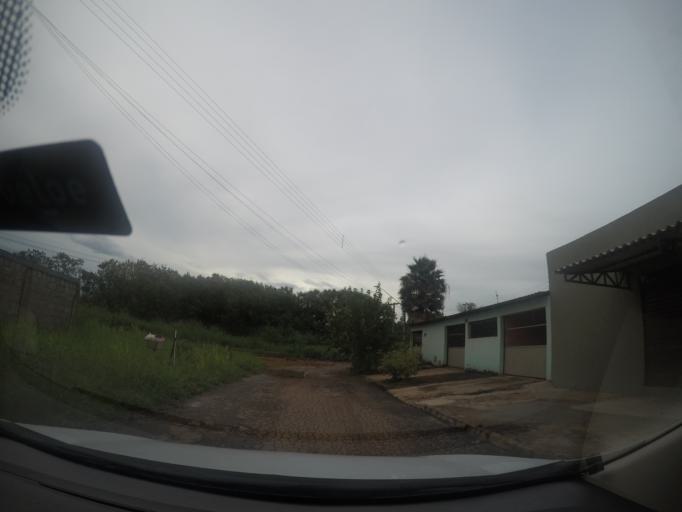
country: BR
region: Goias
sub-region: Goiania
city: Goiania
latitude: -16.6341
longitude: -49.2414
